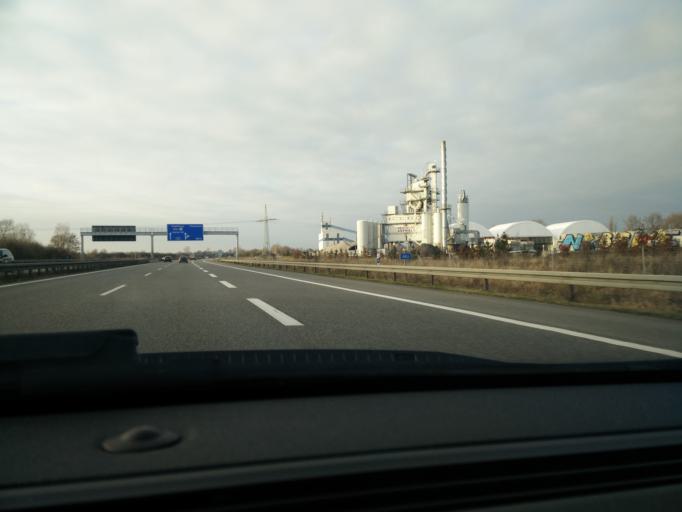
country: DE
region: Saxony
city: Borsdorf
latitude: 51.3143
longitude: 12.5335
